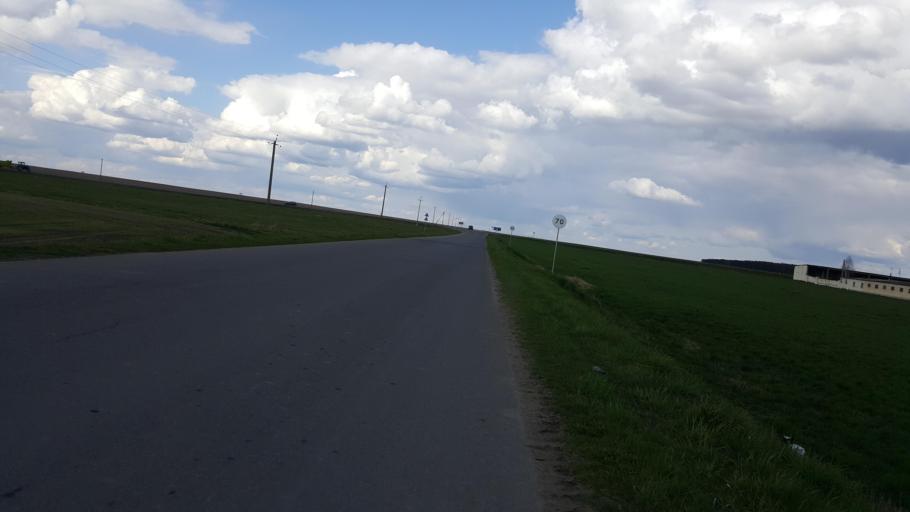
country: BY
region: Brest
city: Kamyanyets
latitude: 52.4153
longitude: 23.6181
